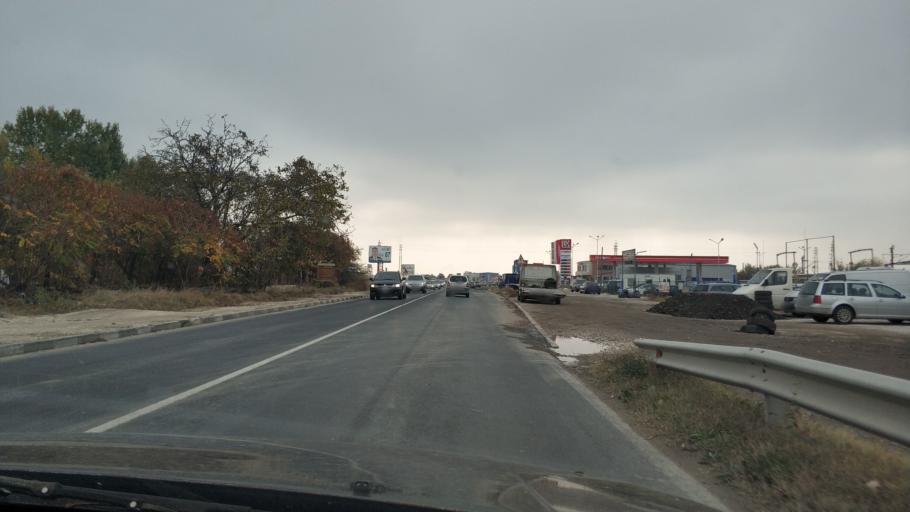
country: BG
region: Plovdiv
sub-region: Obshtina Plovdiv
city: Plovdiv
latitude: 42.2256
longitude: 24.7254
